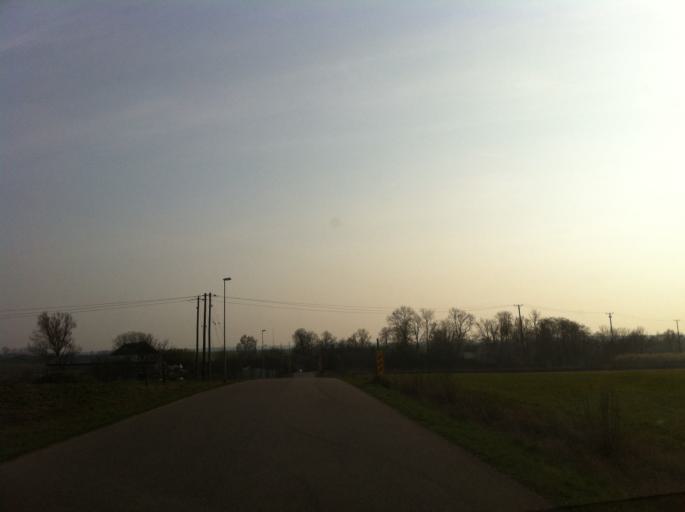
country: SE
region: Skane
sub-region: Svalovs Kommun
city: Teckomatorp
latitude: 55.9024
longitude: 13.0319
